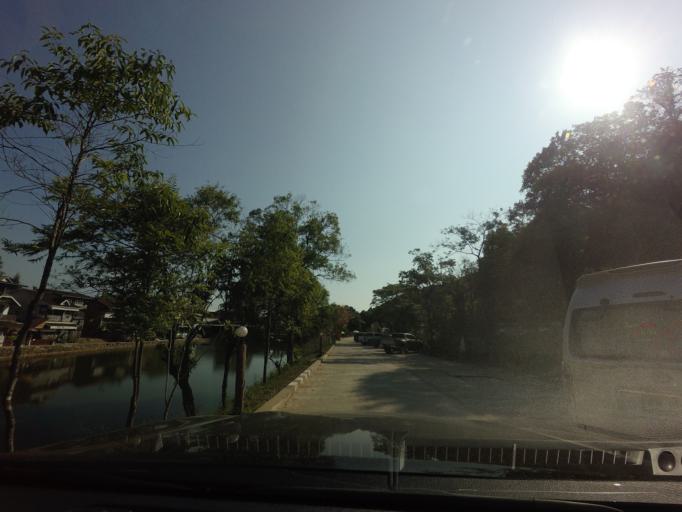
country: TH
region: Kanchanaburi
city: Thong Pha Phum
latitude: 14.6780
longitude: 98.3688
